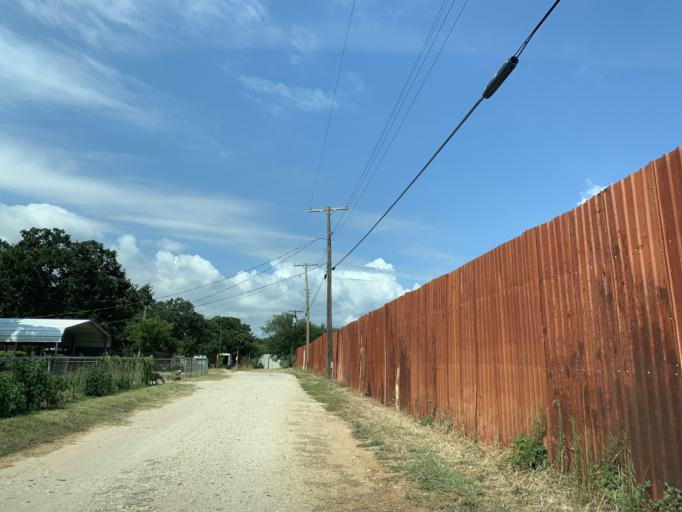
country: US
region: Texas
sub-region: Tarrant County
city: Lakeside
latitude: 32.8343
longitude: -97.4908
